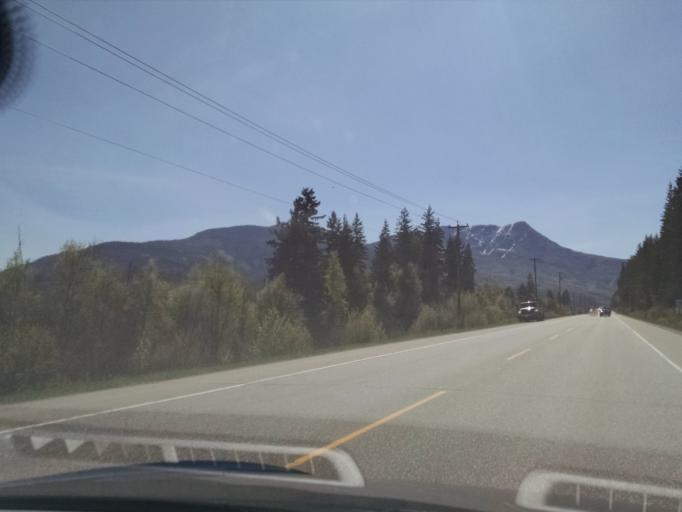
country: CA
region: British Columbia
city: Salmon Arm
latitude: 50.7221
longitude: -119.3170
